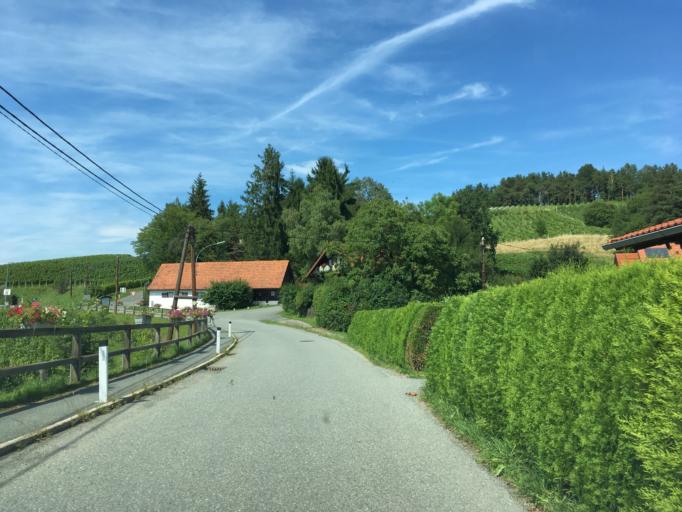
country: AT
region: Styria
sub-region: Politischer Bezirk Leibnitz
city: Kitzeck im Sausal
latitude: 46.7944
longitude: 15.4238
